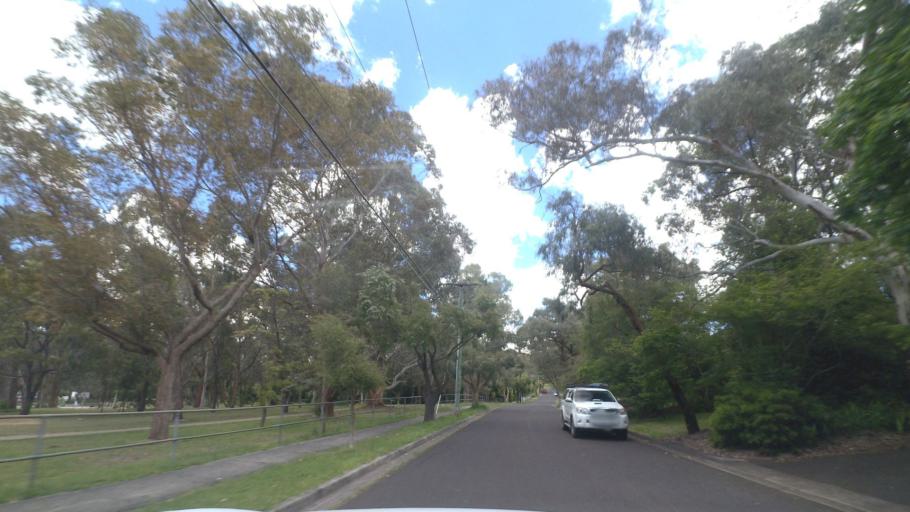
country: AU
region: Victoria
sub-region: Maroondah
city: Croydon South
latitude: -37.8086
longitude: 145.2674
